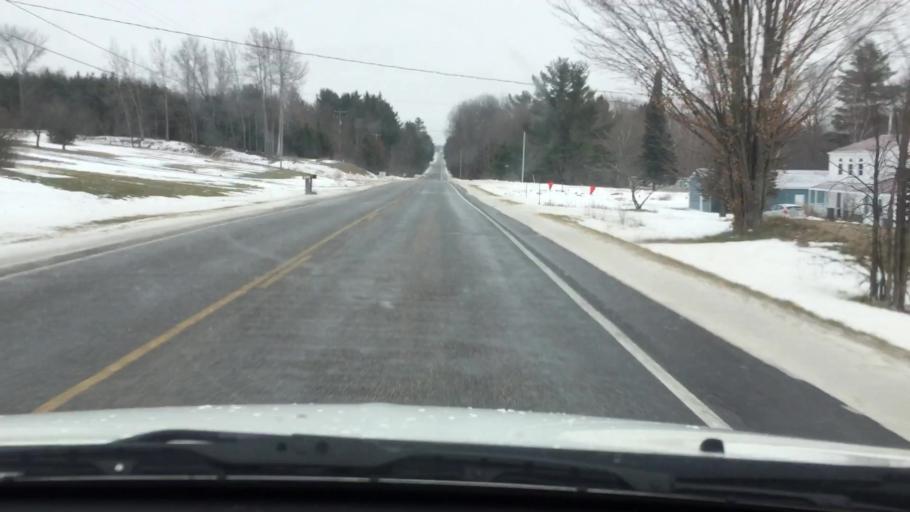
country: US
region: Michigan
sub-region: Wexford County
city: Cadillac
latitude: 44.0608
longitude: -85.4440
